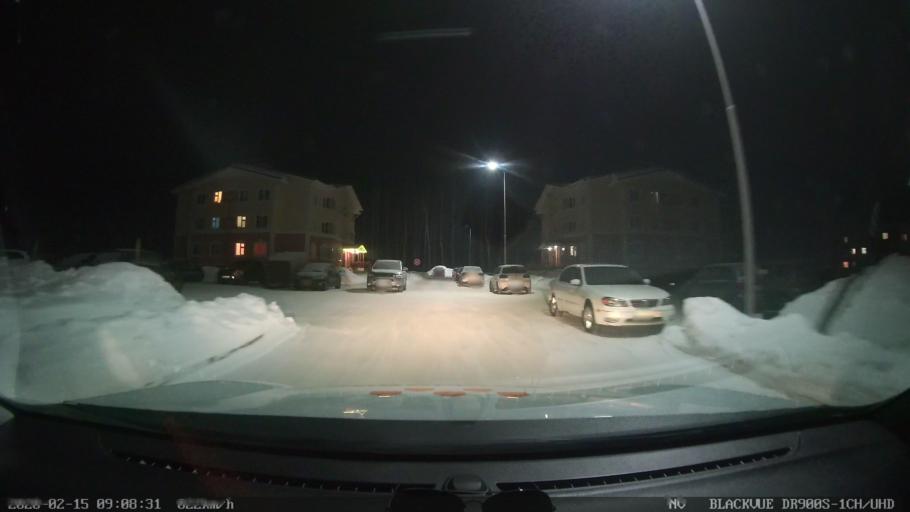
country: RU
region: Tatarstan
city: Stolbishchi
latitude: 55.7040
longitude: 49.3588
